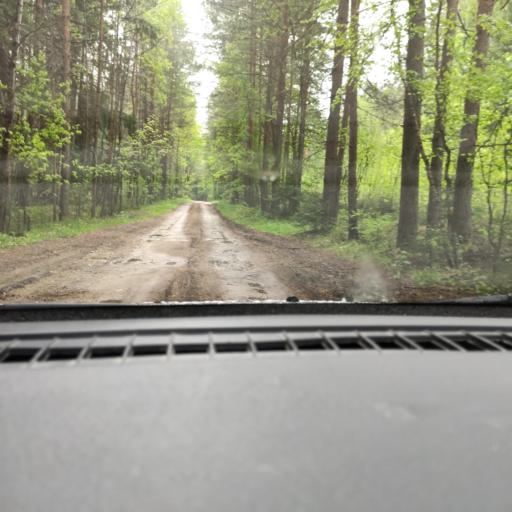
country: RU
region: Perm
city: Overyata
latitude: 58.0161
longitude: 55.8776
